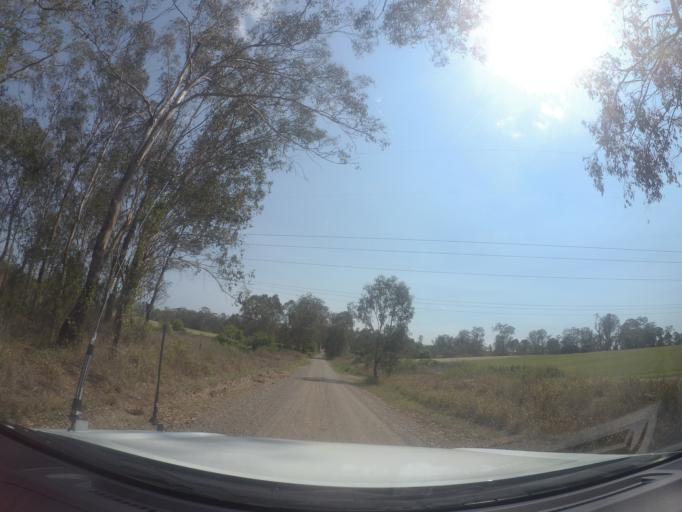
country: AU
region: Queensland
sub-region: Logan
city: North Maclean
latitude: -27.7746
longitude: 153.0381
